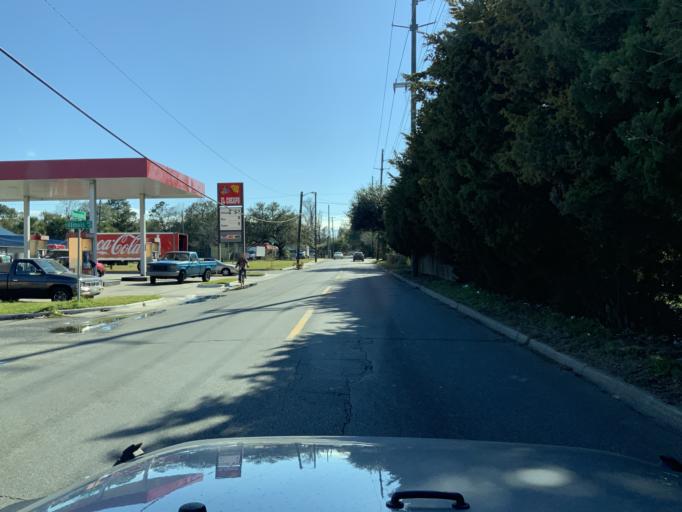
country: US
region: Georgia
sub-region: Chatham County
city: Thunderbolt
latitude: 32.0567
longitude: -81.0621
